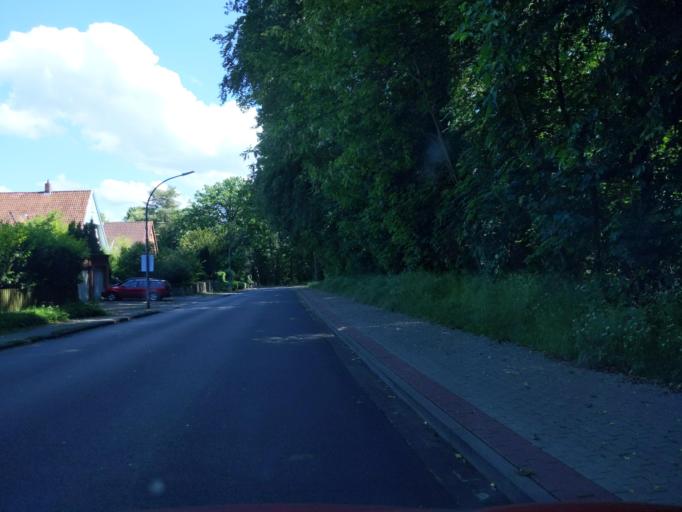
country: DE
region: Lower Saxony
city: Walsrode
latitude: 52.8648
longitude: 9.5784
